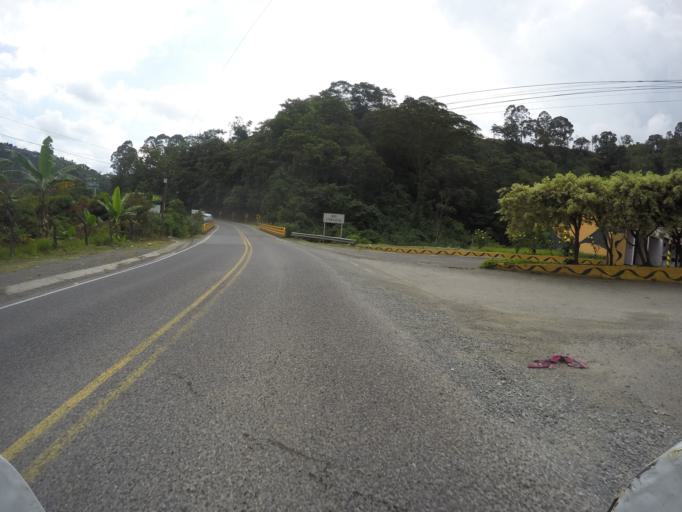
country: CO
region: Risaralda
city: Pereira
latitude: 4.7868
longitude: -75.6938
